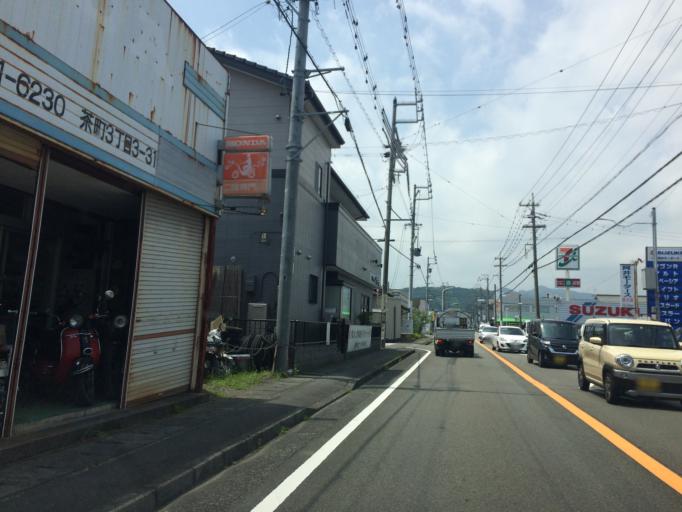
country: JP
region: Shizuoka
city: Fujieda
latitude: 34.8726
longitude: 138.2427
